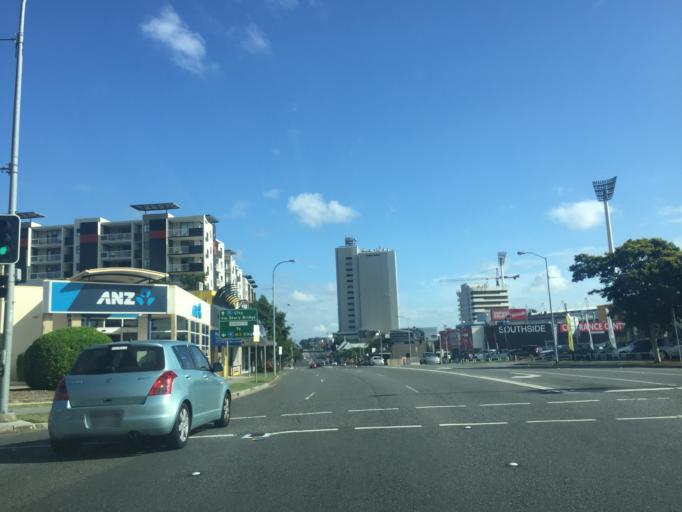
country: AU
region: Queensland
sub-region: Brisbane
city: Woolloongabba
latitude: -27.4886
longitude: 153.0359
